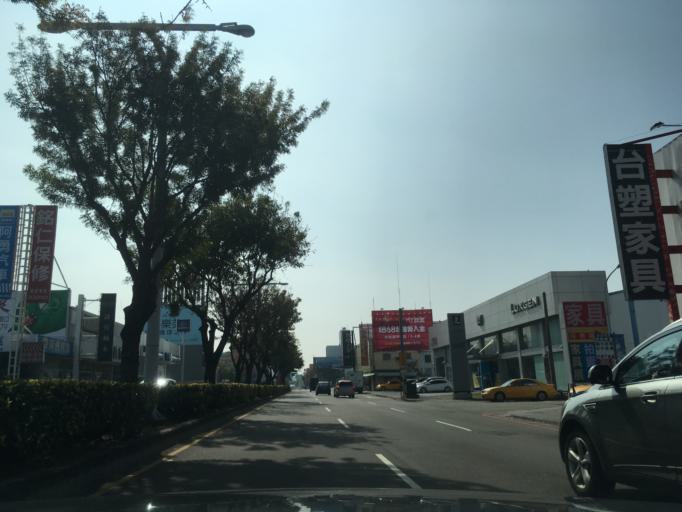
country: TW
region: Taiwan
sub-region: Taichung City
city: Taichung
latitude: 24.1986
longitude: 120.6565
